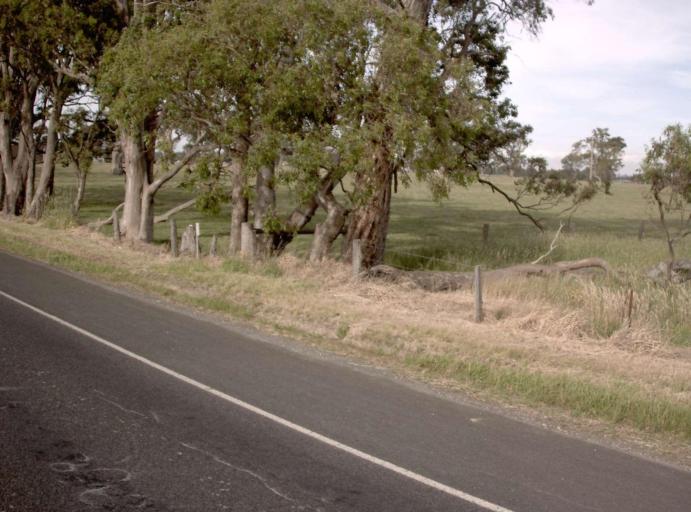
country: AU
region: Victoria
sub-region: Latrobe
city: Traralgon
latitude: -38.1441
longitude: 146.5559
